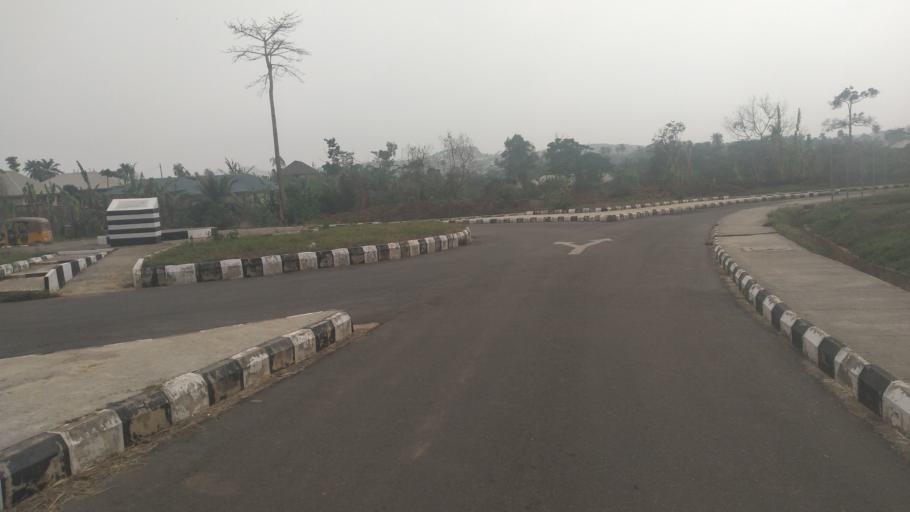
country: NG
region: Ondo
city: Ilare
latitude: 7.2951
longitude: 5.1355
